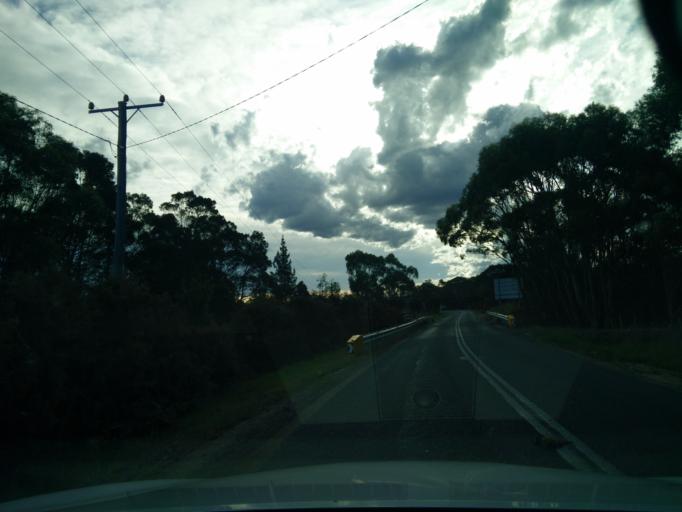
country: AU
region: Tasmania
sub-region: Break O'Day
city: St Helens
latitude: -41.9426
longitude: 148.2167
